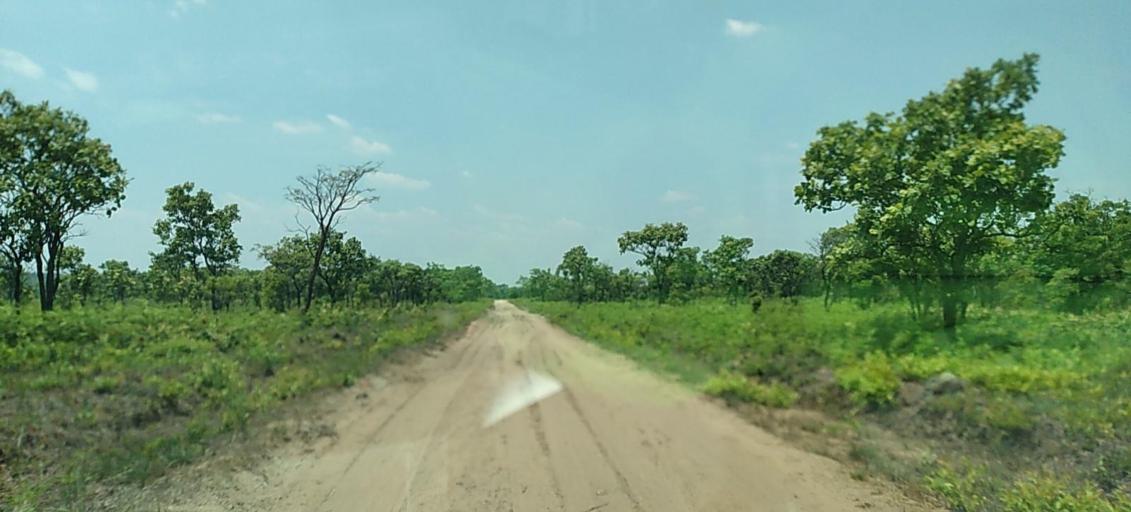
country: CD
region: Katanga
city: Kolwezi
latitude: -11.3373
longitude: 25.2228
